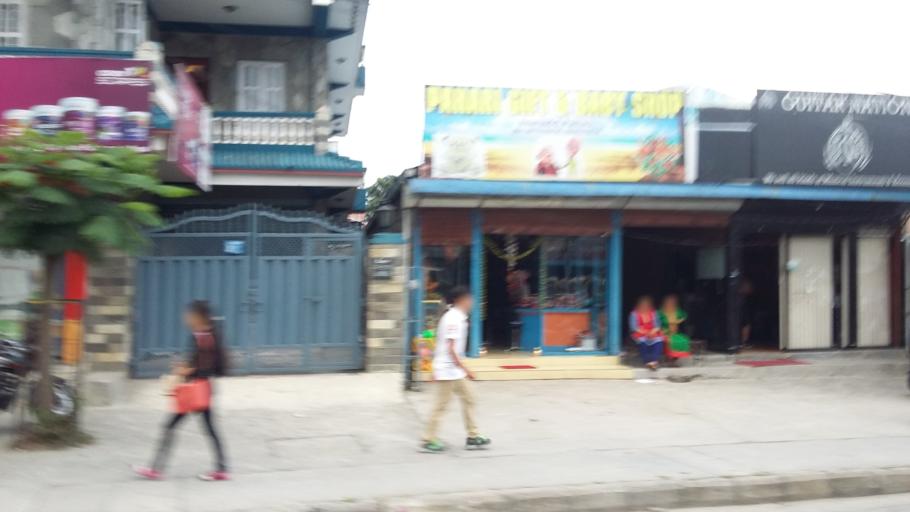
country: NP
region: Western Region
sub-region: Gandaki Zone
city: Pokhara
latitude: 28.2148
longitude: 83.9859
